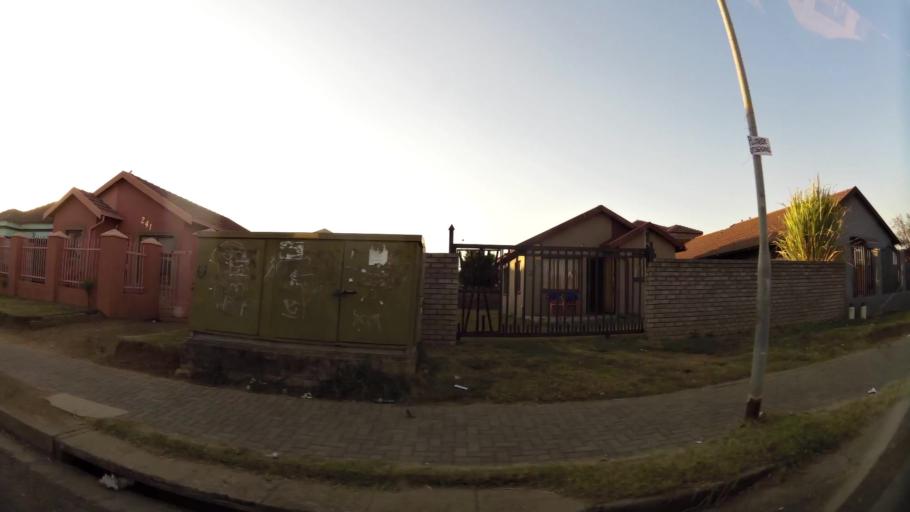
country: ZA
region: Gauteng
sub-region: City of Tshwane Metropolitan Municipality
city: Pretoria
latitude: -25.7476
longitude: 28.1164
